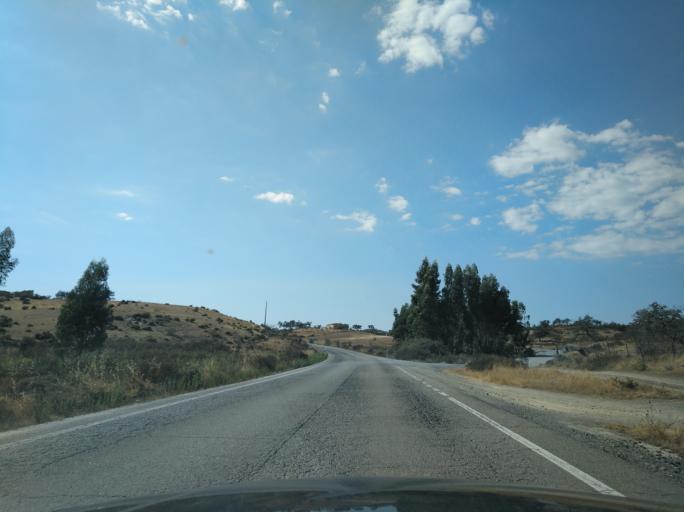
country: ES
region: Andalusia
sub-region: Provincia de Huelva
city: Santa Barbara de Casa
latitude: 37.7869
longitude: -7.1666
